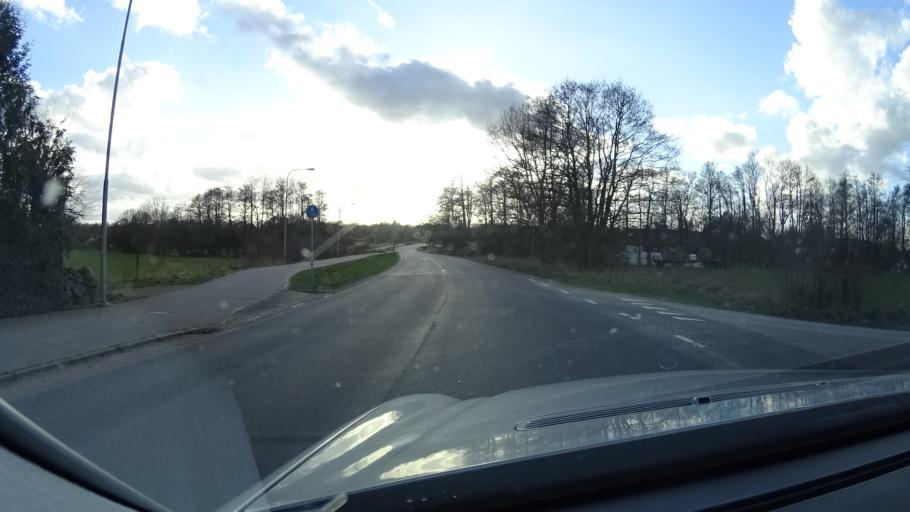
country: SE
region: Skane
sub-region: Hoors Kommun
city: Satofta
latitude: 55.9084
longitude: 13.5623
